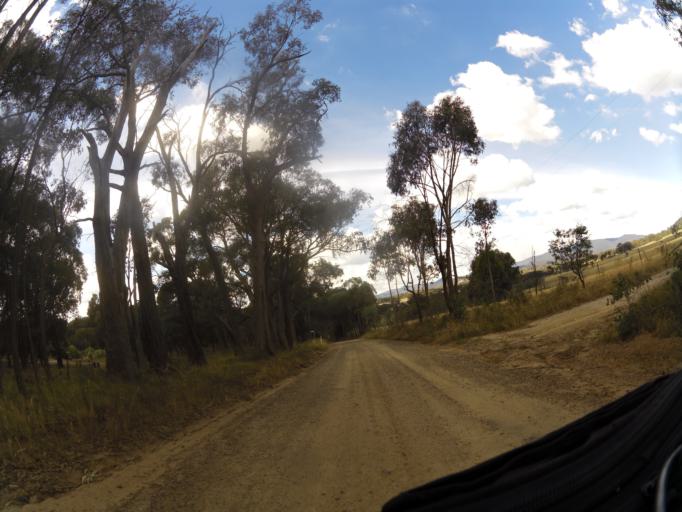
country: AU
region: Victoria
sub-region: Benalla
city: Benalla
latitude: -36.7818
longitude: 145.9884
